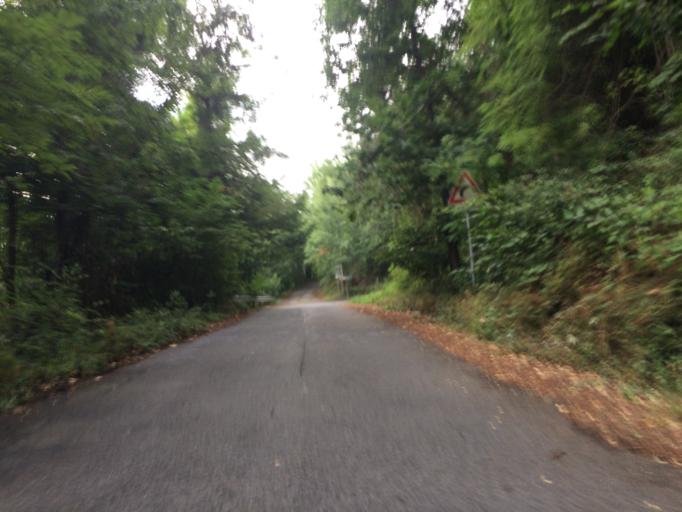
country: IT
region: Liguria
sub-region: Provincia di Imperia
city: Triora
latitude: 43.9844
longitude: 7.7623
